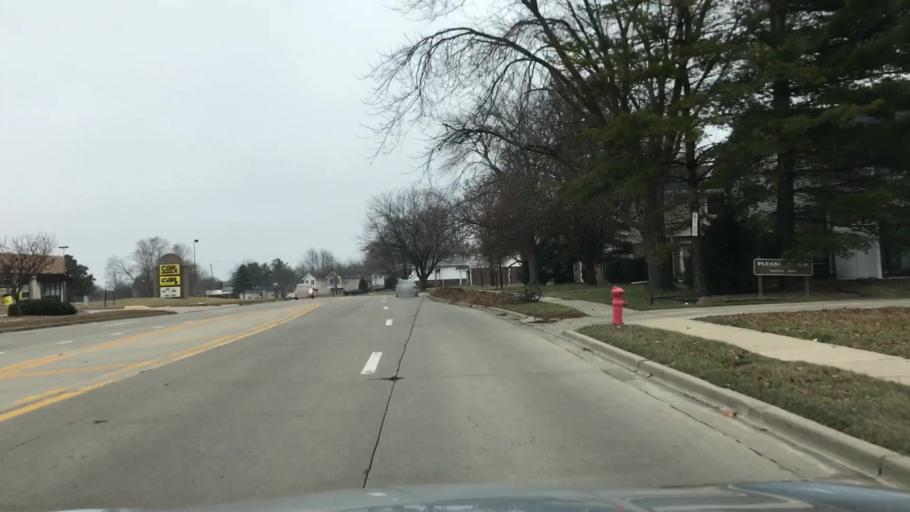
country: US
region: Illinois
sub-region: McLean County
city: Normal
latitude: 40.5095
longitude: -88.9607
